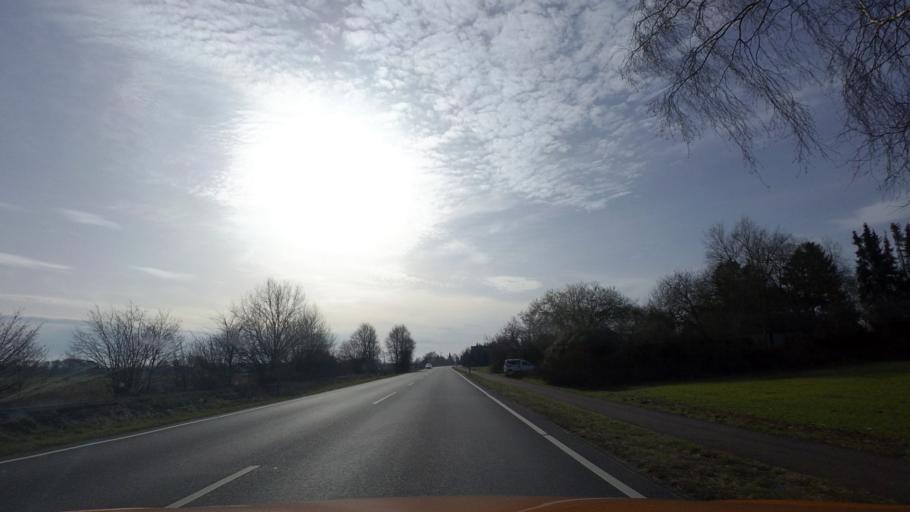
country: DE
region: Lower Saxony
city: Neuenkirchen
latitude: 52.7699
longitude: 8.7593
